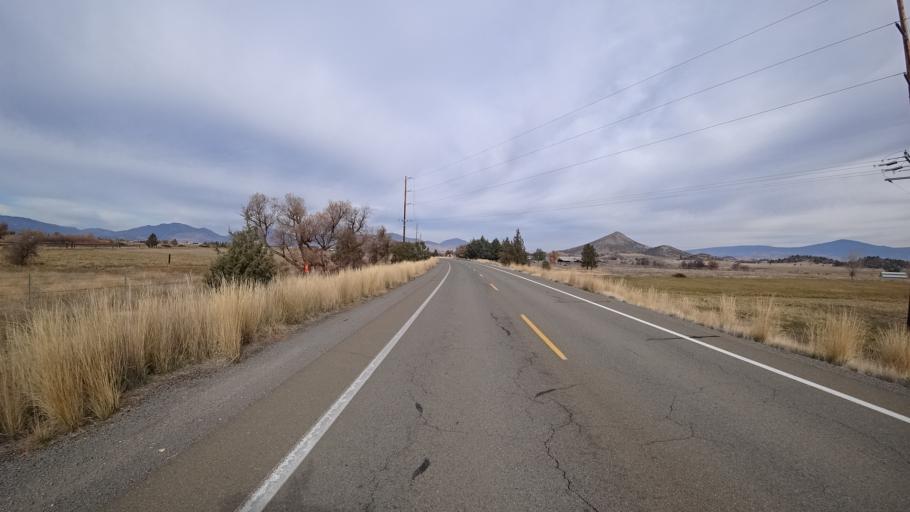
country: US
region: California
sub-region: Siskiyou County
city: Montague
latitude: 41.6893
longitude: -122.5351
